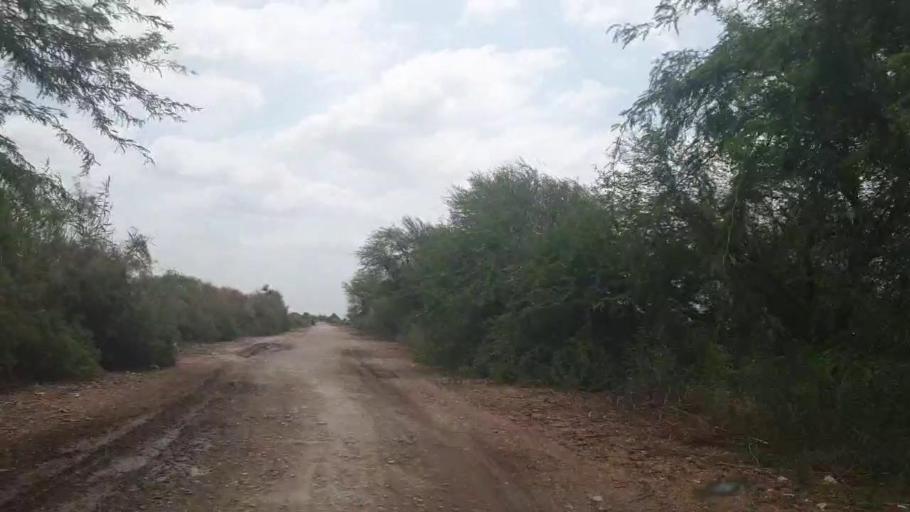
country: PK
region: Sindh
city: Tando Mittha Khan
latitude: 25.8872
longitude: 69.1430
